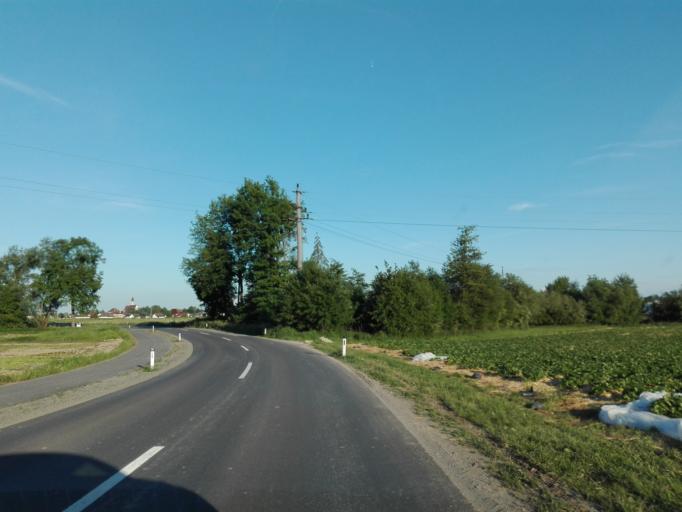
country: AT
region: Upper Austria
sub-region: Politischer Bezirk Urfahr-Umgebung
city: Feldkirchen an der Donau
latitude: 48.3184
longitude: 14.0005
